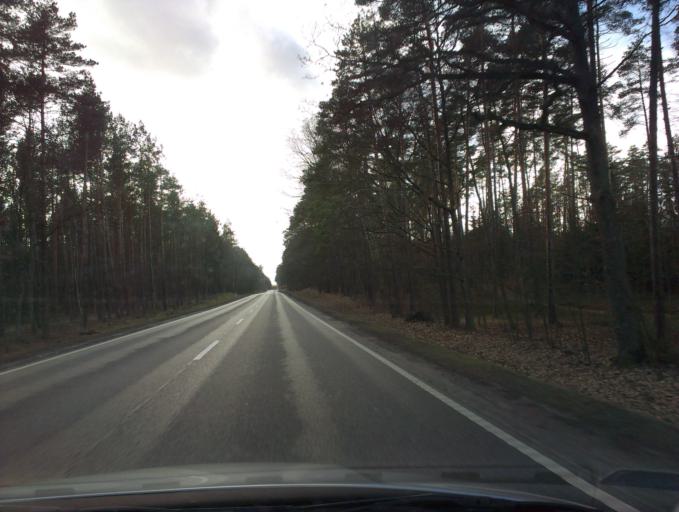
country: PL
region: Pomeranian Voivodeship
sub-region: Powiat czluchowski
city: Czluchow
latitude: 53.6472
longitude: 17.3076
